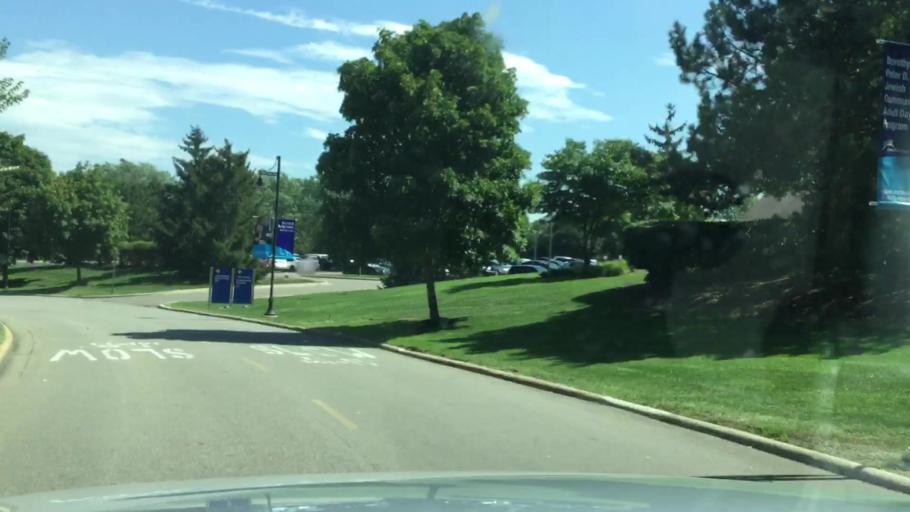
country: US
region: Michigan
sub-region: Oakland County
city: West Bloomfield Township
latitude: 42.5432
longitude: -83.4057
